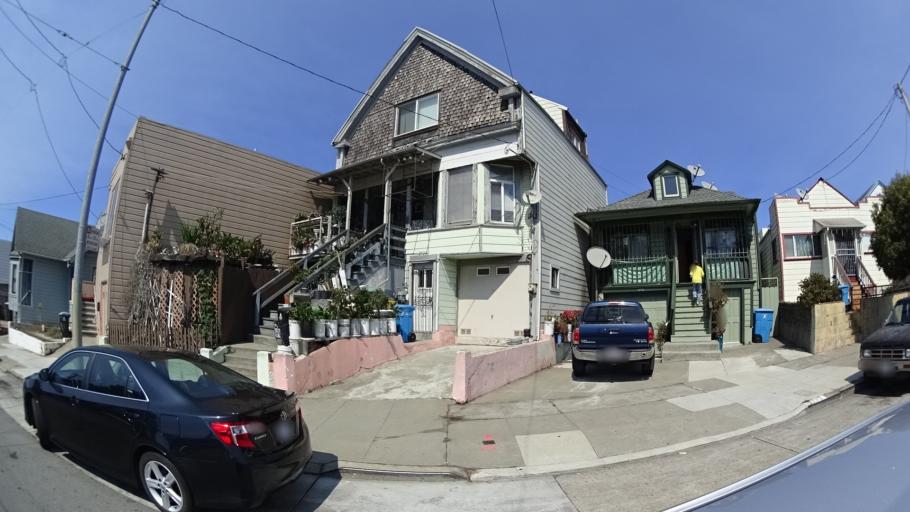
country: US
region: California
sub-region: San Mateo County
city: Daly City
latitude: 37.7136
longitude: -122.4528
